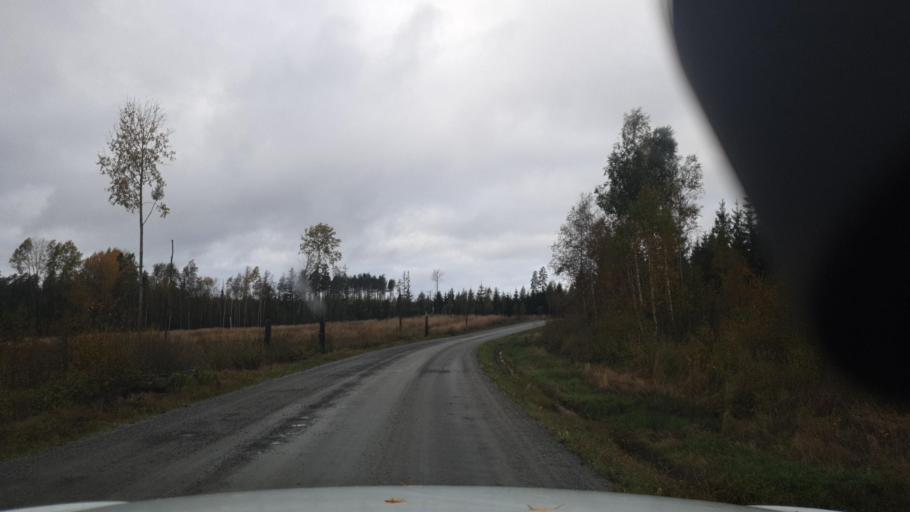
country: SE
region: Vaermland
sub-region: Karlstads Kommun
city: Edsvalla
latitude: 59.4428
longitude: 13.1696
